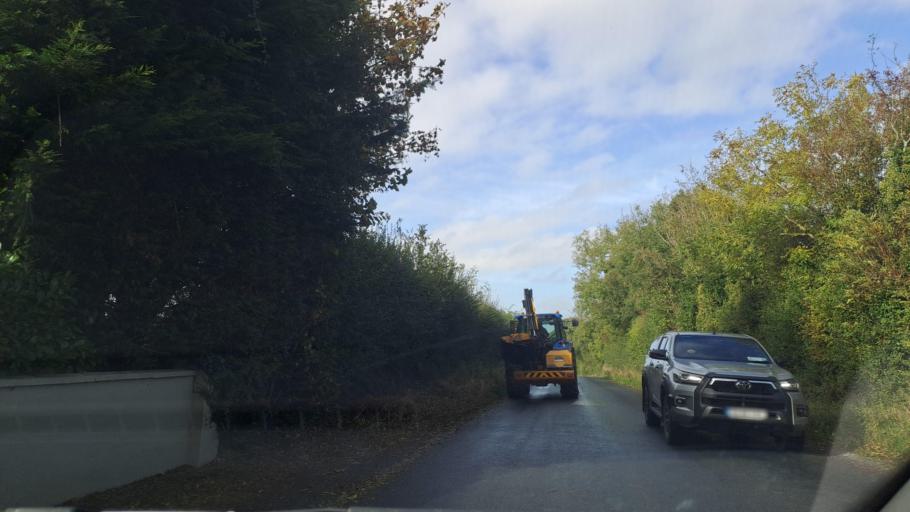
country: IE
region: Ulster
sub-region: County Monaghan
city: Carrickmacross
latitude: 53.8729
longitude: -6.6673
